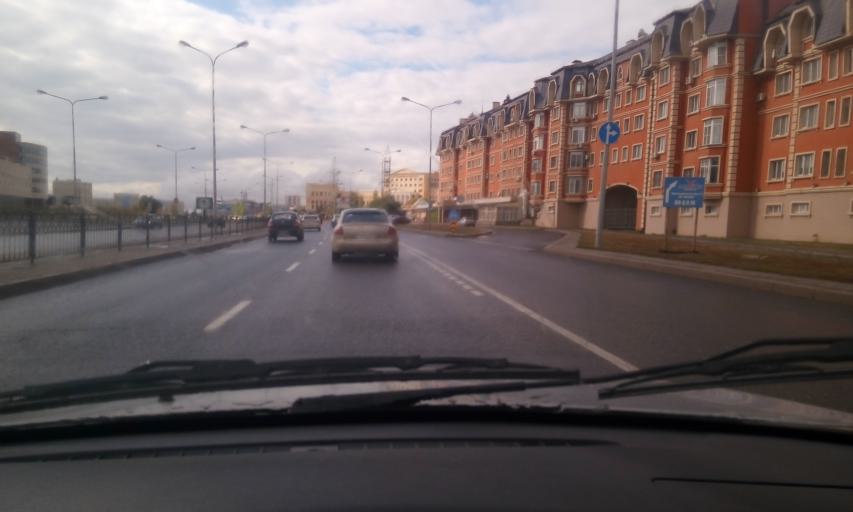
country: KZ
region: Astana Qalasy
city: Astana
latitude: 51.1487
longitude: 71.3870
